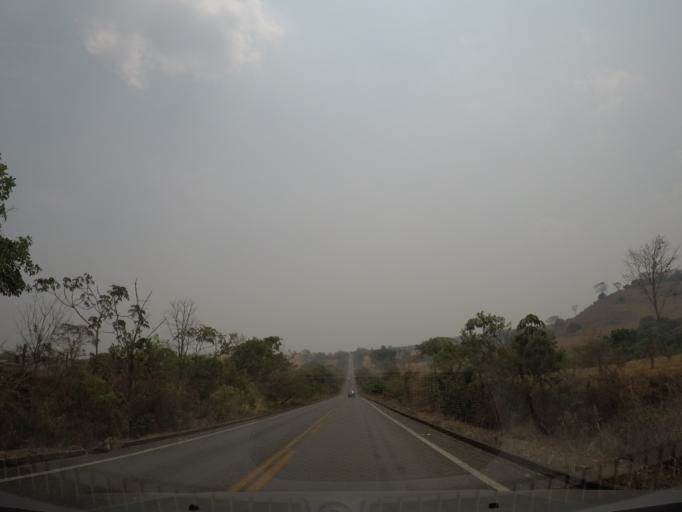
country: BR
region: Goias
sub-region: Pirenopolis
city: Pirenopolis
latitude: -15.8984
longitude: -48.8737
